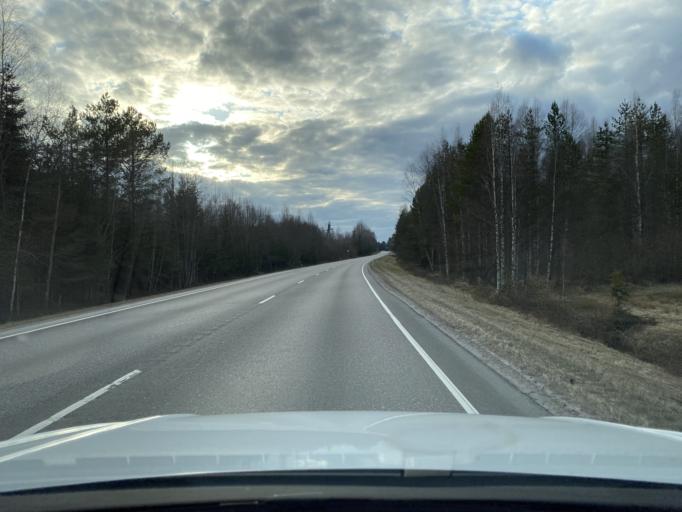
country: FI
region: Haeme
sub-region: Haemeenlinna
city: Renko
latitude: 60.7871
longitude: 24.1362
